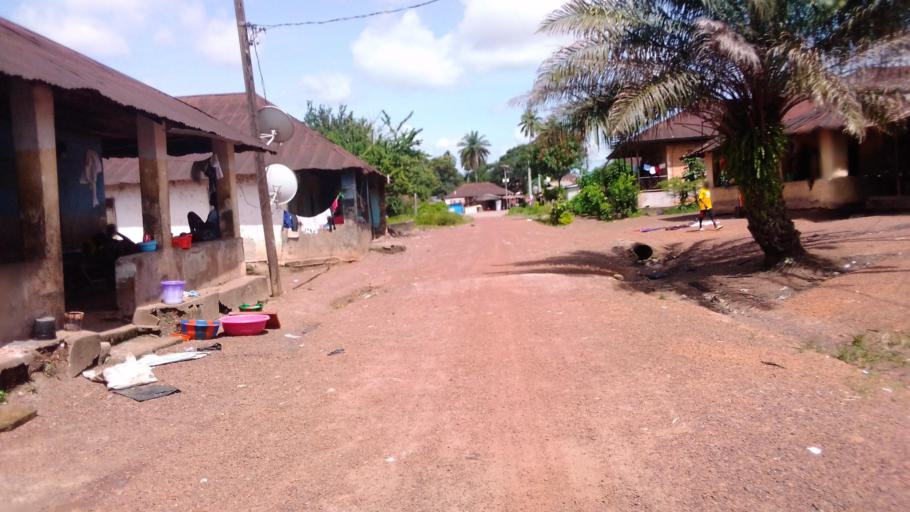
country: SL
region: Northern Province
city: Makeni
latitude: 8.8842
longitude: -12.0455
